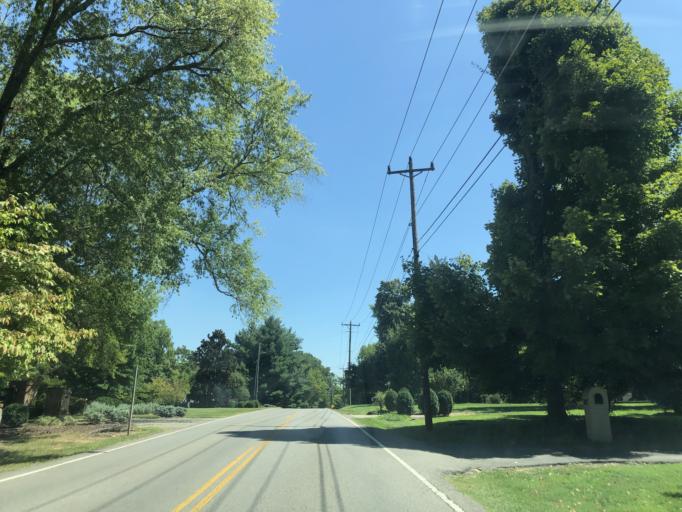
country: US
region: Tennessee
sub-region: Davidson County
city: Oak Hill
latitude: 36.0803
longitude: -86.7952
